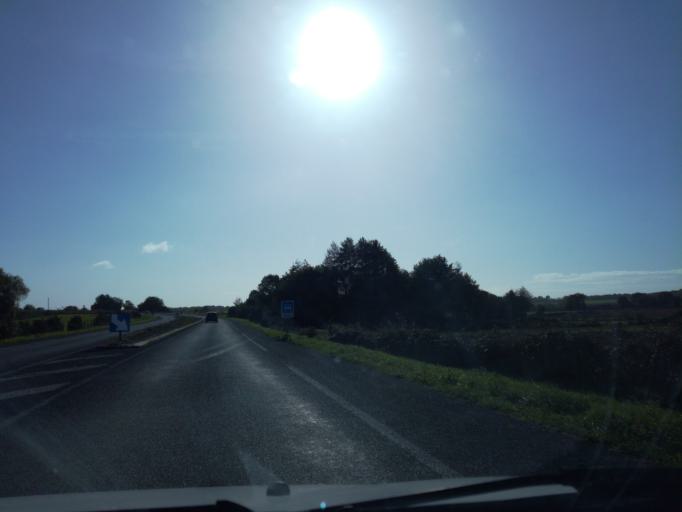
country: FR
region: Pays de la Loire
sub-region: Departement de Maine-et-Loire
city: Pouance
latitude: 47.7646
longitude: -1.2136
